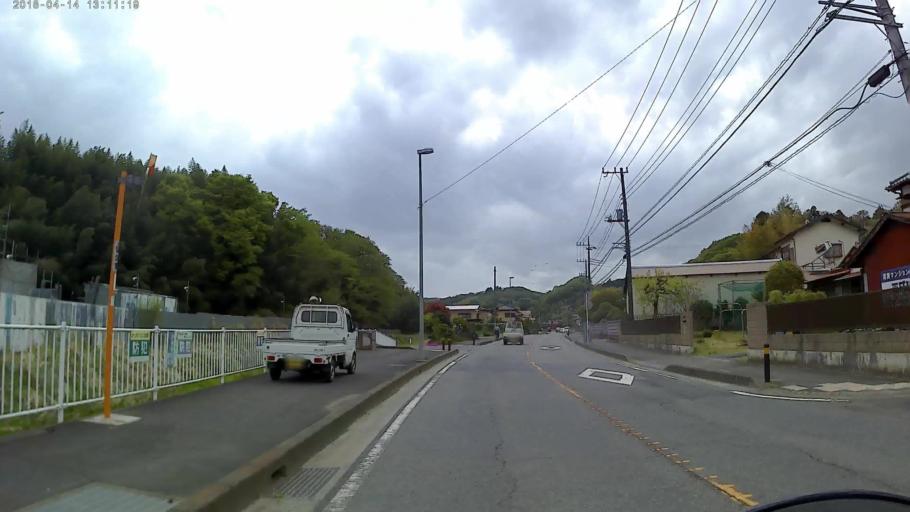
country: JP
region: Kanagawa
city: Hadano
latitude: 35.3475
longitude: 139.2569
